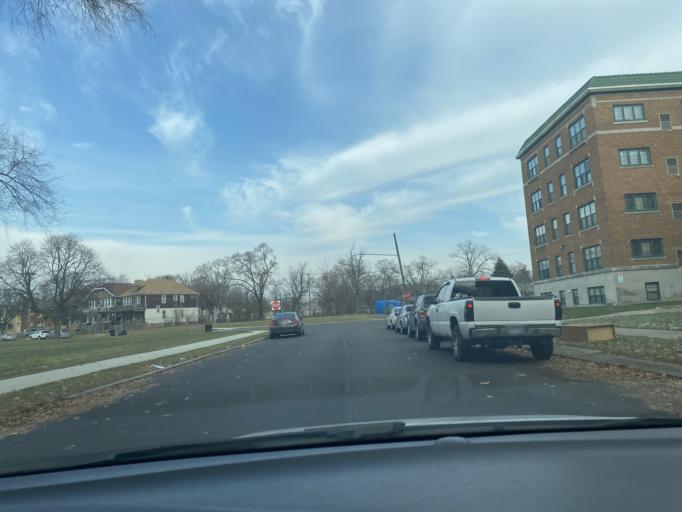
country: US
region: Michigan
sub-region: Wayne County
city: Highland Park
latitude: 42.3679
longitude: -83.1317
